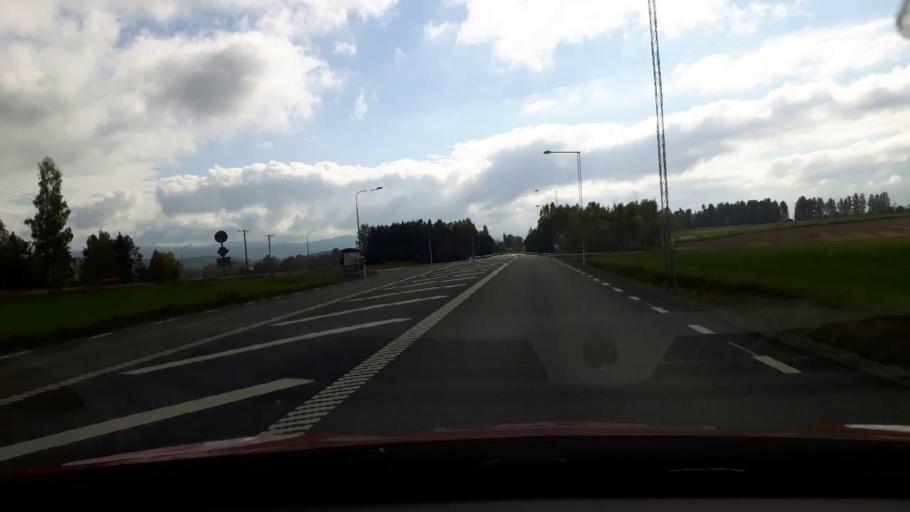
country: SE
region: Gaevleborg
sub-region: Bollnas Kommun
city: Arbra
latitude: 61.5419
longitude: 16.3566
